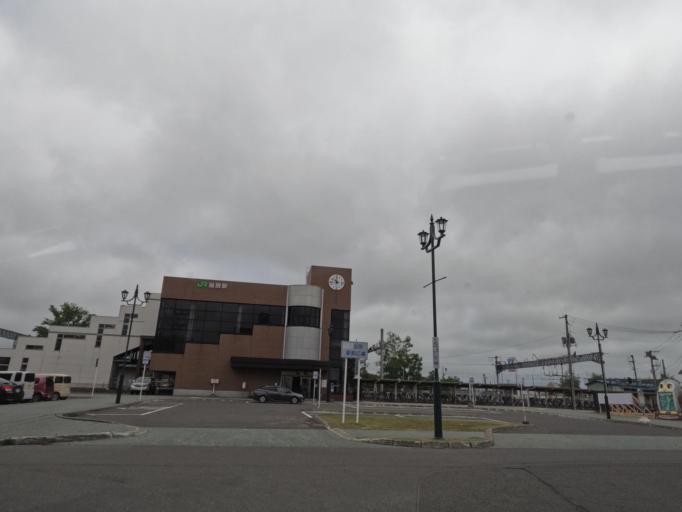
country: JP
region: Hokkaido
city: Tobetsu
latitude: 43.2217
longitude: 141.5149
